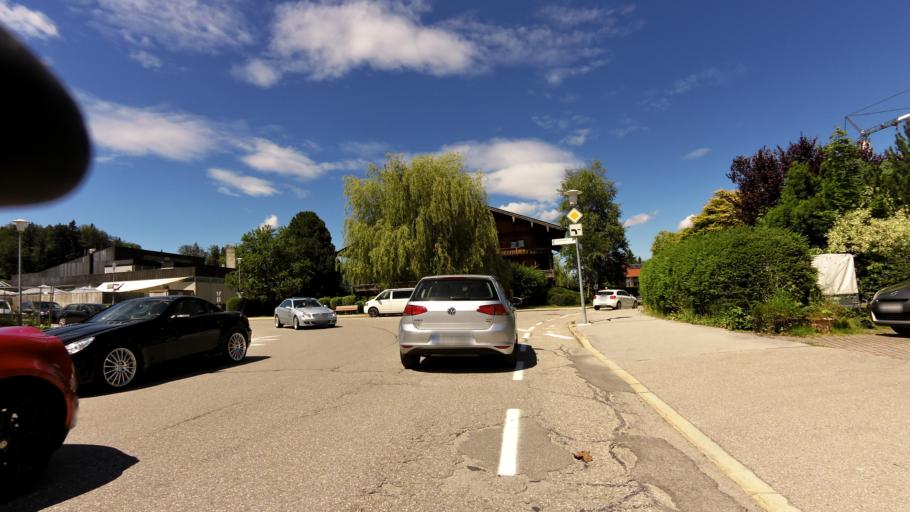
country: DE
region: Bavaria
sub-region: Upper Bavaria
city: Bad Wiessee
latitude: 47.7197
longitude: 11.7247
